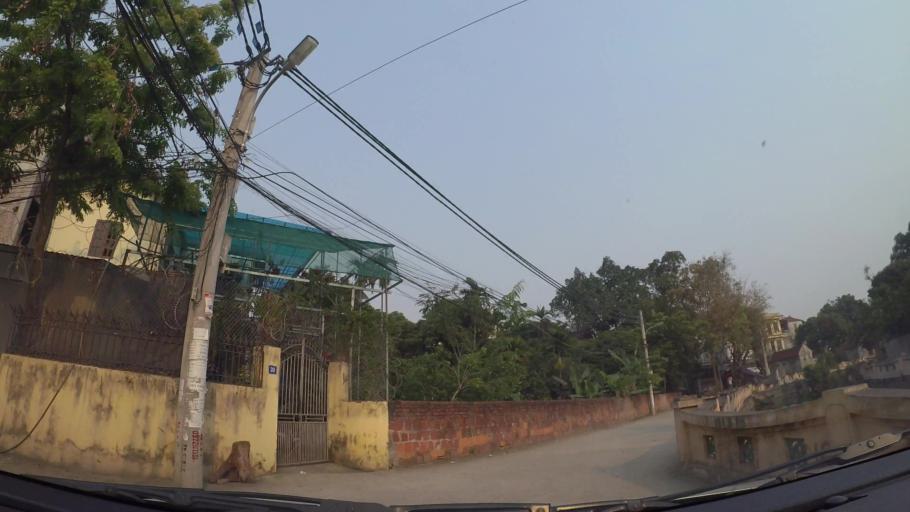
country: VN
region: Ha Noi
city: Cau Dien
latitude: 21.0027
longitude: 105.7460
